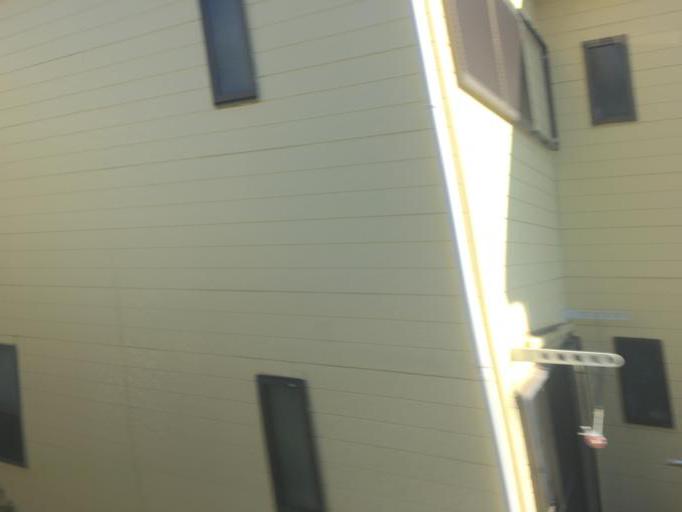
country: JP
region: Chiba
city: Matsudo
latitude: 35.7465
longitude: 139.8776
